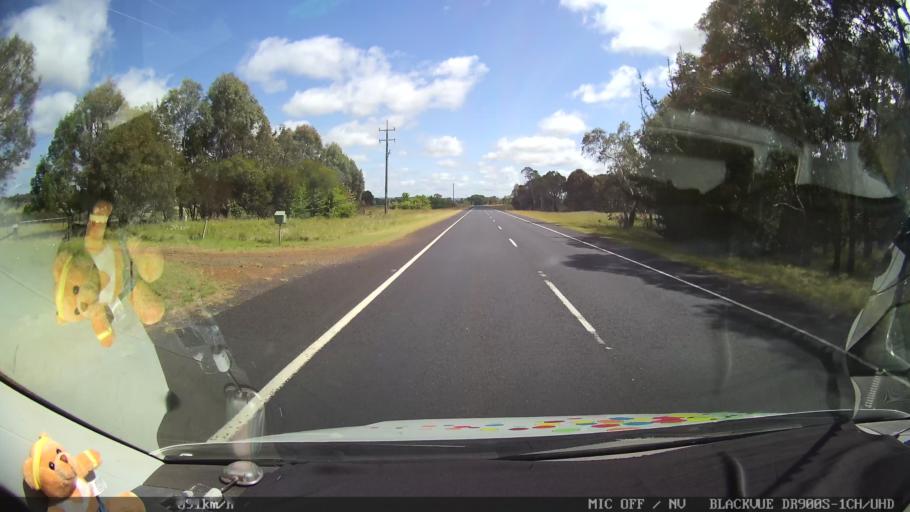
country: AU
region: New South Wales
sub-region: Glen Innes Severn
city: Glen Innes
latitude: -29.8687
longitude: 151.7362
